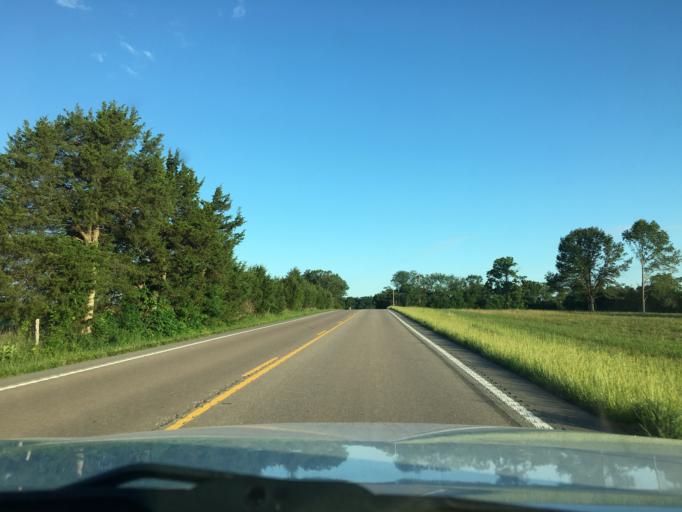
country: US
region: Missouri
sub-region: Gasconade County
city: Owensville
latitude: 38.4534
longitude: -91.4547
